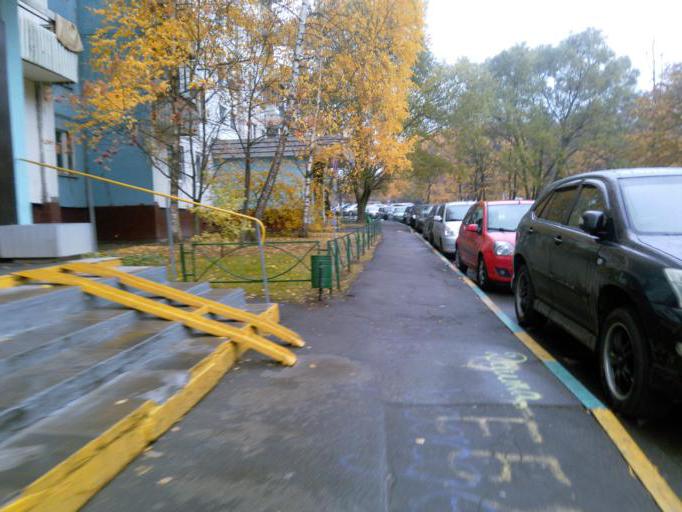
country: RU
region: Moscow
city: Yasenevo
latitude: 55.6022
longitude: 37.5103
